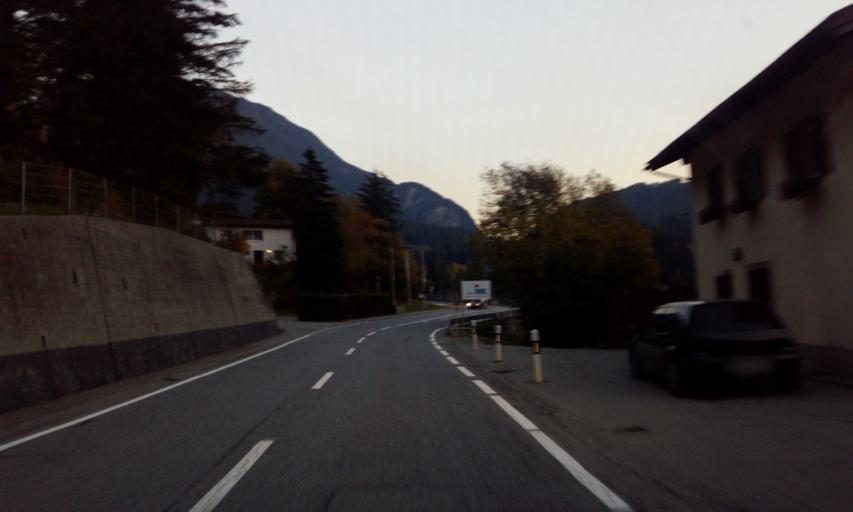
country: CH
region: Grisons
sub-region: Albula District
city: Tiefencastel
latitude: 46.6658
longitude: 9.5710
